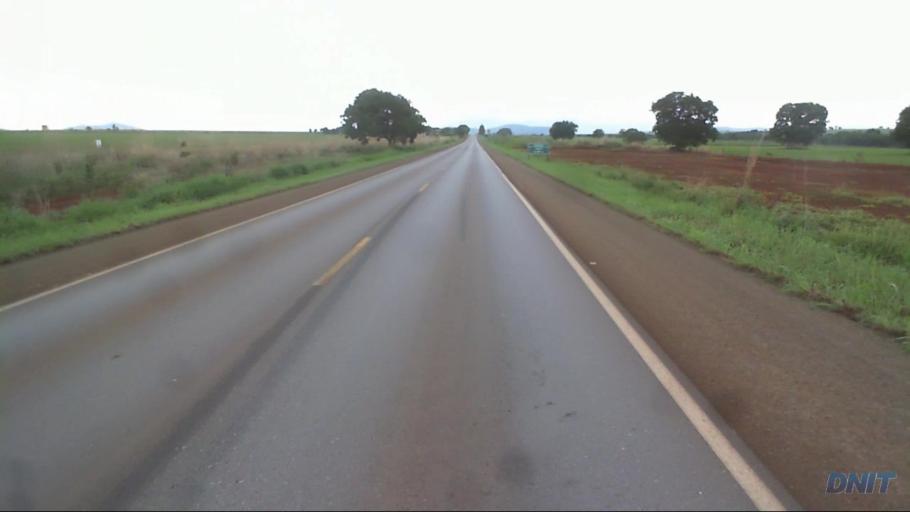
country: BR
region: Goias
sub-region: Barro Alto
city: Barro Alto
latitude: -14.8287
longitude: -49.0356
